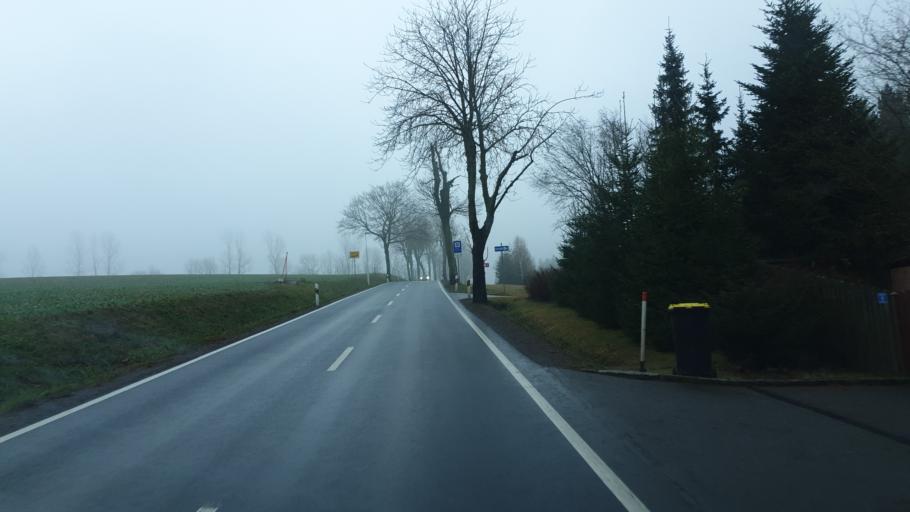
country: DE
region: Saxony
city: Sayda
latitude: 50.7089
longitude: 13.4304
